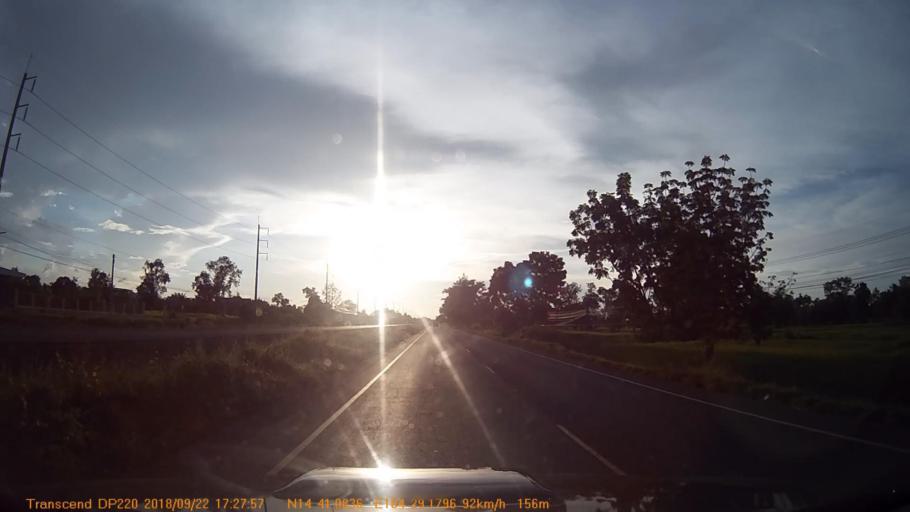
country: TH
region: Sisaket
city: Khun Han
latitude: 14.6848
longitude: 104.4859
